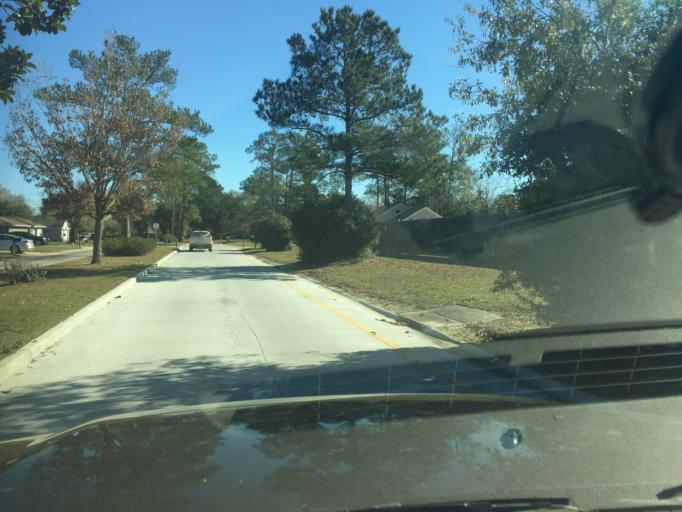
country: US
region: Louisiana
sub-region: Saint Tammany Parish
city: Slidell
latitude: 30.2994
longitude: -89.7427
